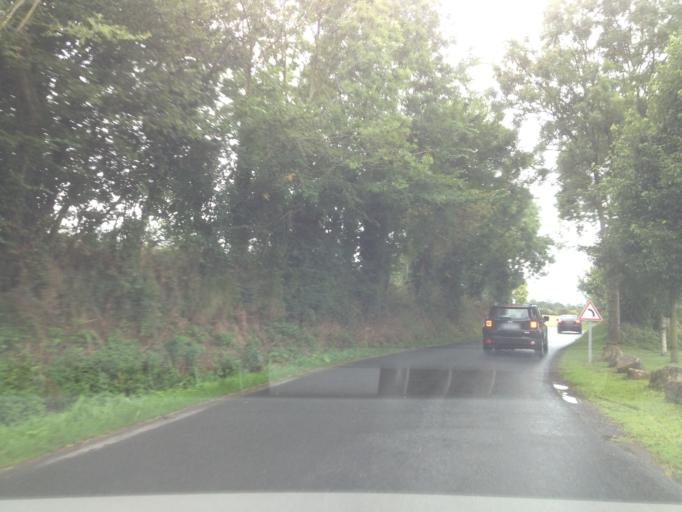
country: FR
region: Lower Normandy
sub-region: Departement du Calvados
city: Bayeux
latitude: 49.3022
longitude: -0.7036
